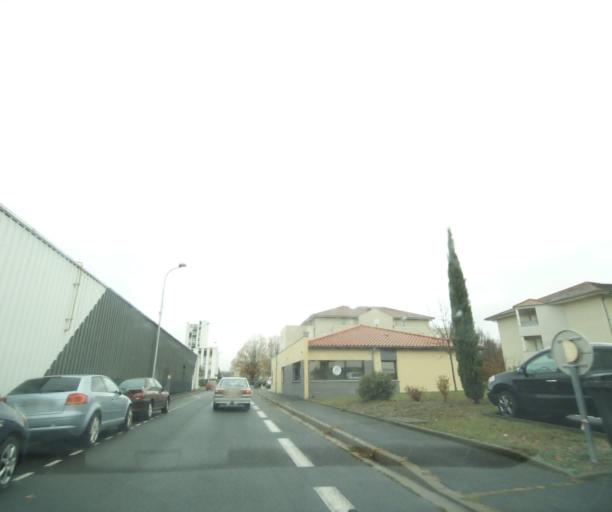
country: FR
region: Auvergne
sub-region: Departement du Puy-de-Dome
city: Cournon-d'Auvergne
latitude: 45.7319
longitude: 3.1948
